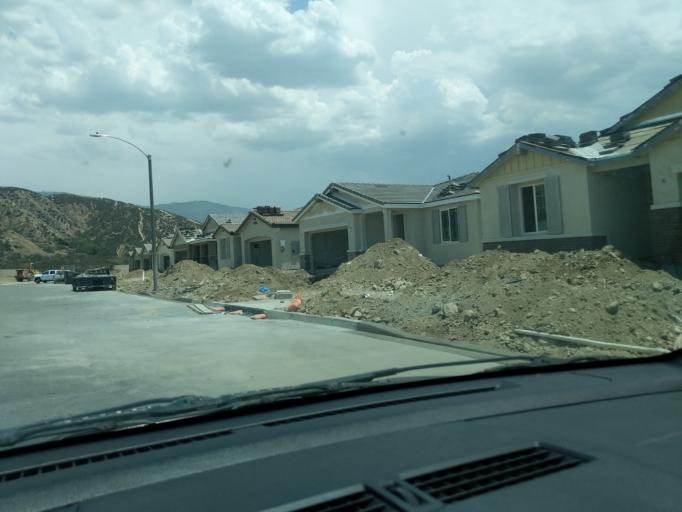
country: US
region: California
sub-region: San Bernardino County
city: Muscoy
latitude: 34.1854
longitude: -117.4059
